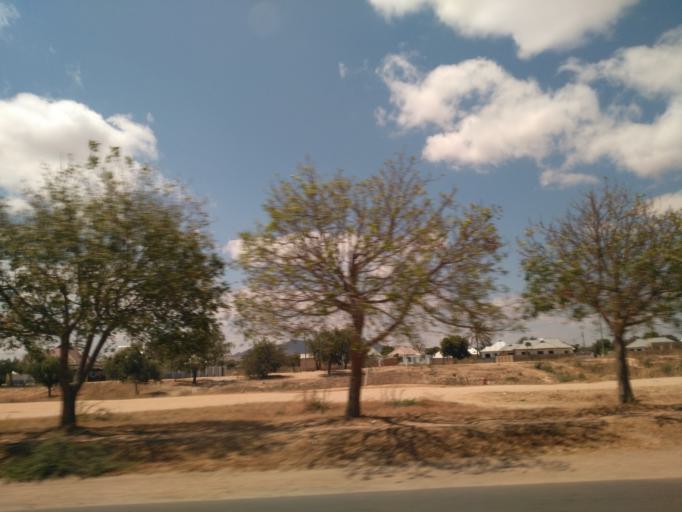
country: TZ
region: Dodoma
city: Kisasa
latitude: -6.1711
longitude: 35.7713
